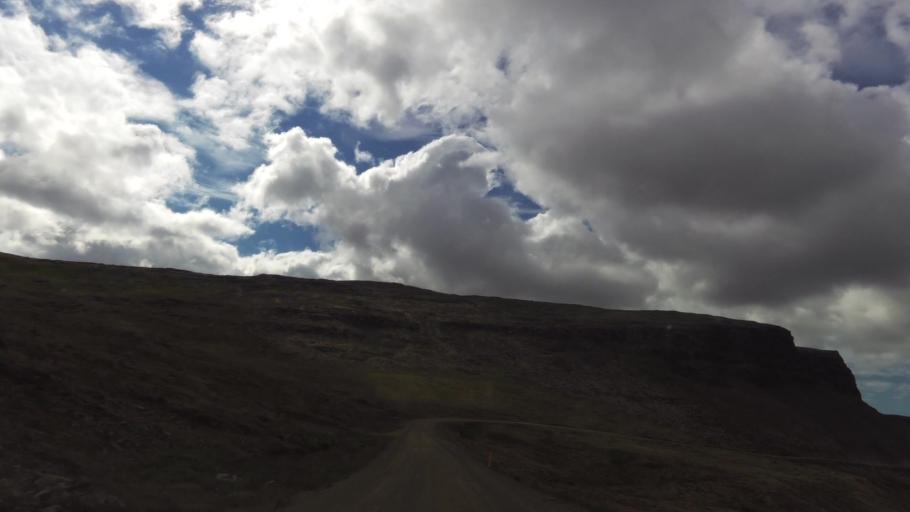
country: IS
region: West
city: Olafsvik
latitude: 65.5614
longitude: -24.0284
